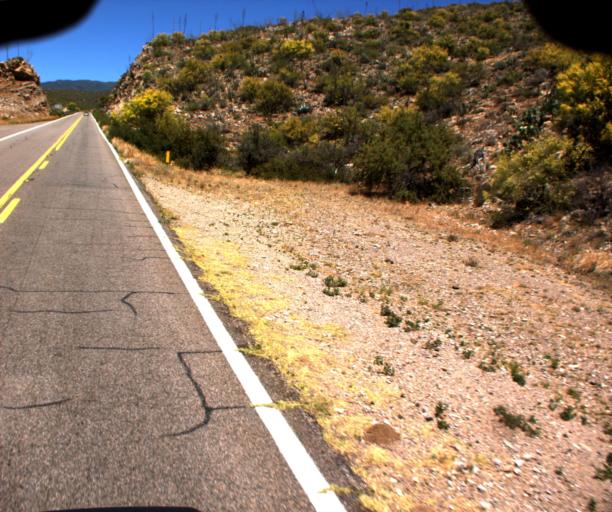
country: US
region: Arizona
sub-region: Pinal County
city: Kearny
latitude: 33.1783
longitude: -110.8111
